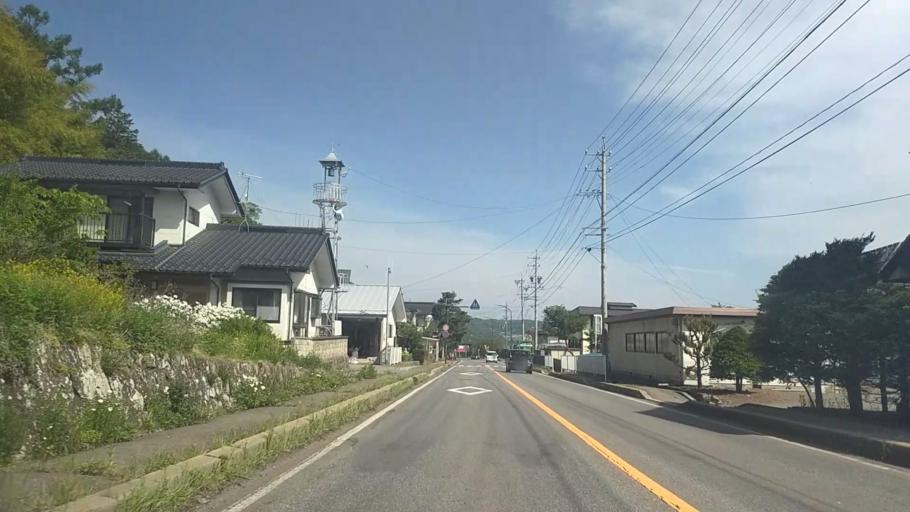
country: JP
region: Nagano
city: Saku
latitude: 36.1086
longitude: 138.4783
